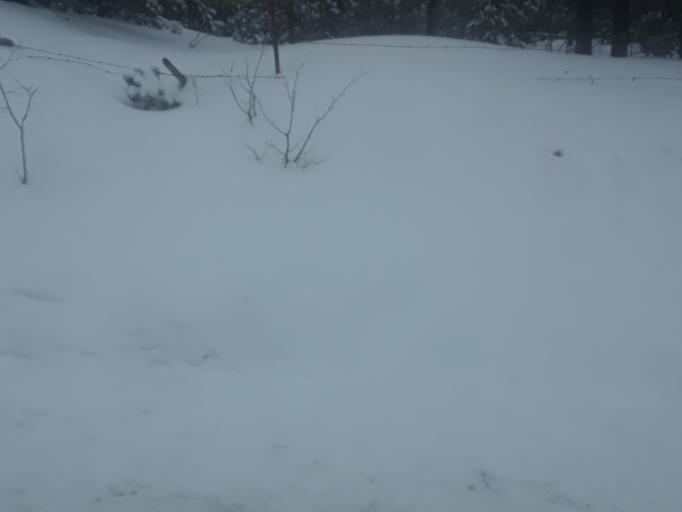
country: US
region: Colorado
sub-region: Boulder County
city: Coal Creek
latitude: 39.9260
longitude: -105.4029
